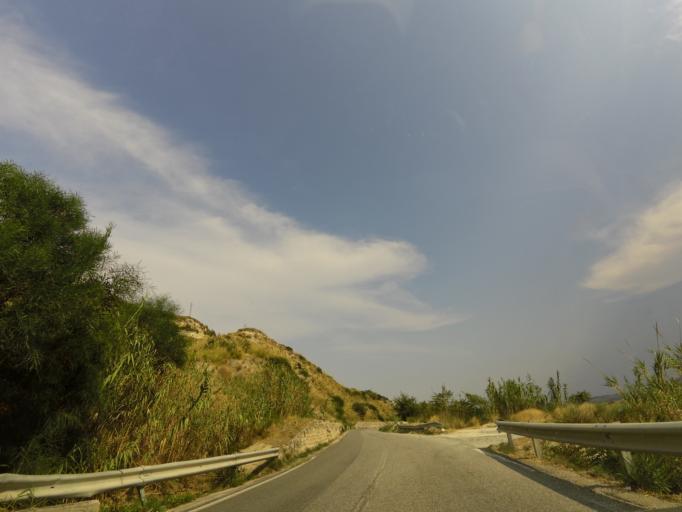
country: IT
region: Calabria
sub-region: Provincia di Reggio Calabria
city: Monasterace
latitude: 38.4638
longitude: 16.5144
